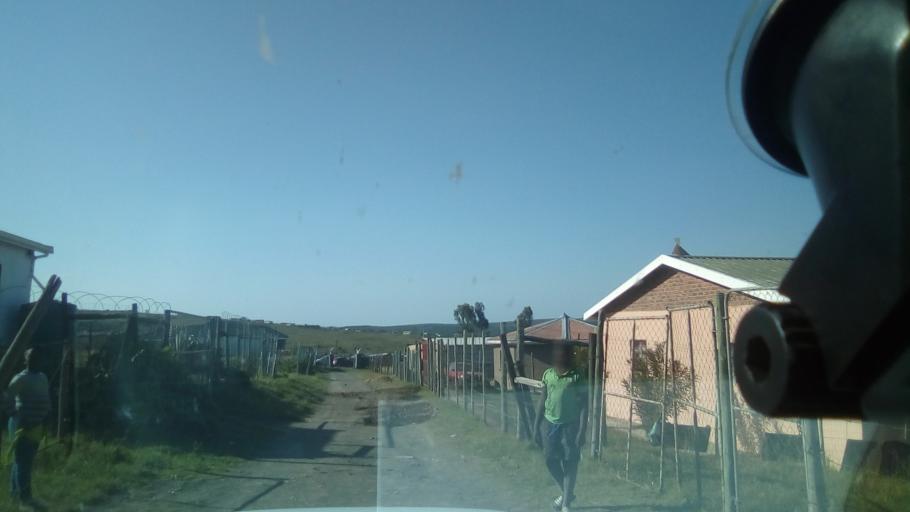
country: ZA
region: Eastern Cape
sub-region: Buffalo City Metropolitan Municipality
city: Bhisho
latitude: -32.8115
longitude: 27.3562
